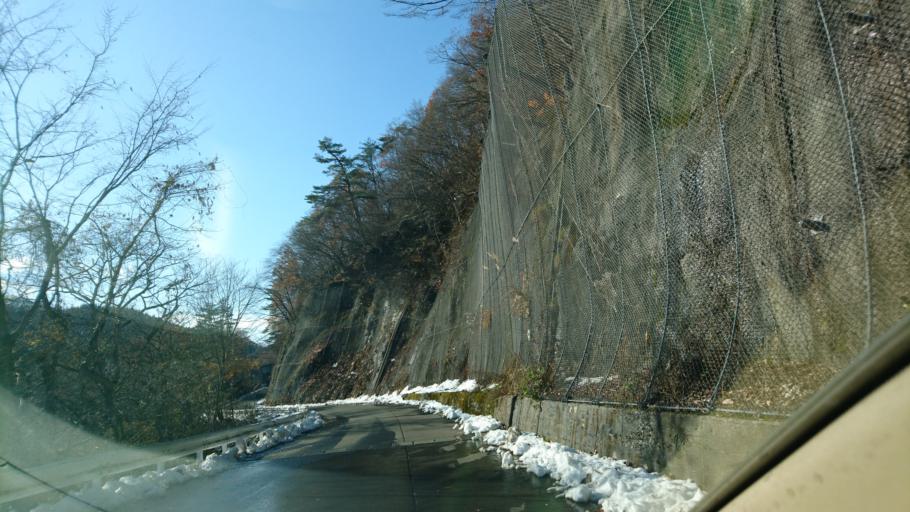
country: JP
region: Akita
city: Yokotemachi
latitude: 39.3112
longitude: 140.7693
